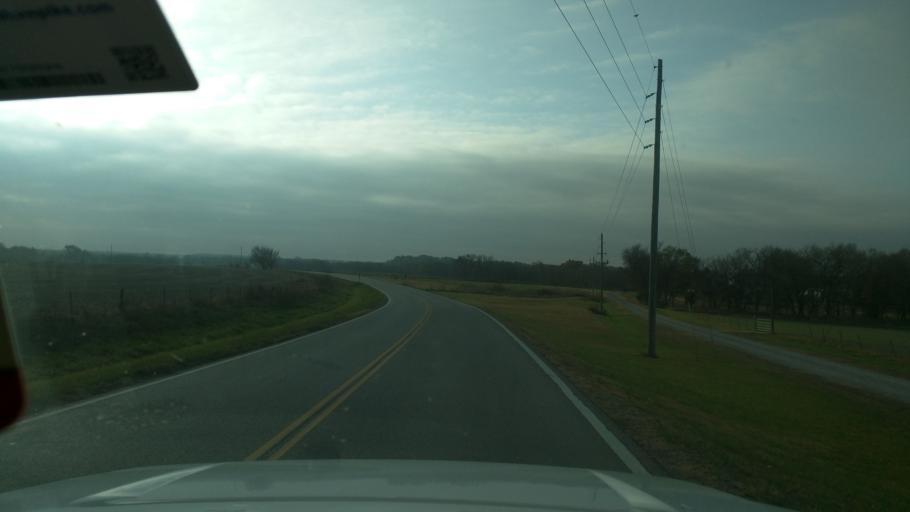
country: US
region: Kansas
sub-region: Greenwood County
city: Eureka
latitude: 37.7513
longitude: -96.2343
